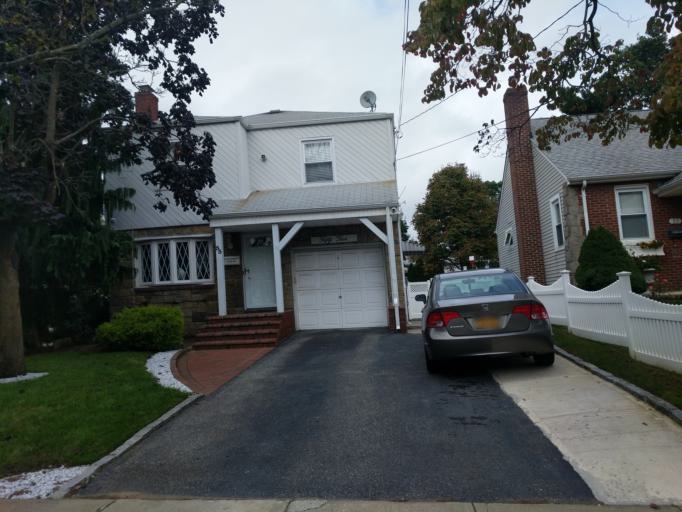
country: US
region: New York
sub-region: Nassau County
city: Valley Stream
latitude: 40.6676
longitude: -73.6942
